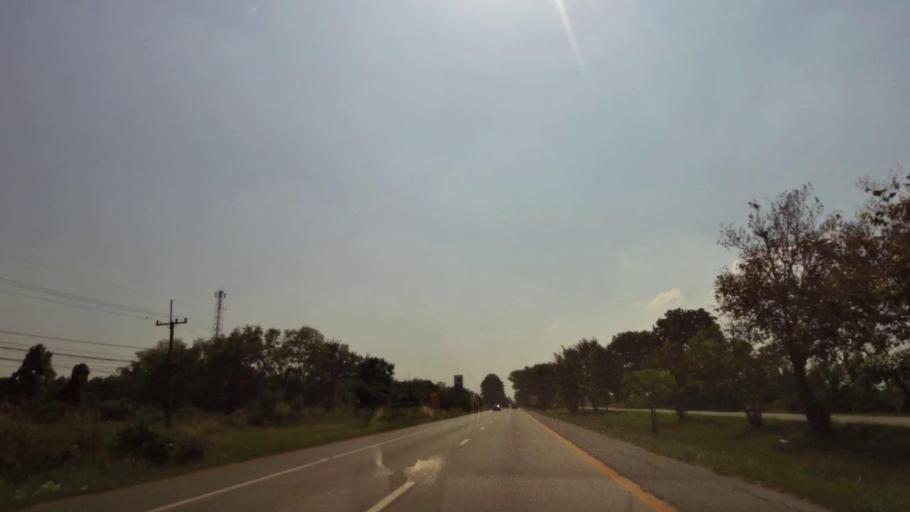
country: TH
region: Phichit
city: Wachira Barami
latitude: 16.5827
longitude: 100.1475
